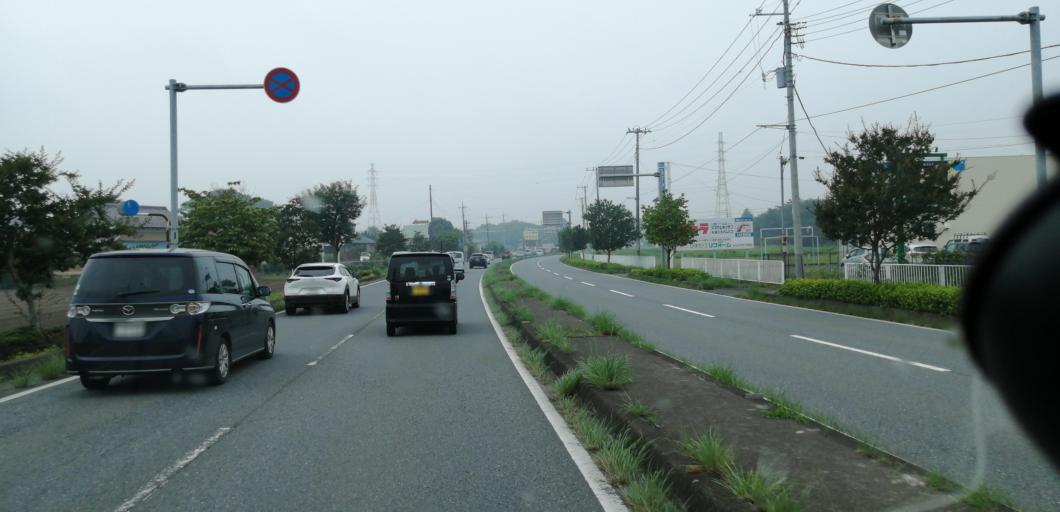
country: JP
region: Saitama
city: Yorii
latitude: 36.1291
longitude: 139.2515
